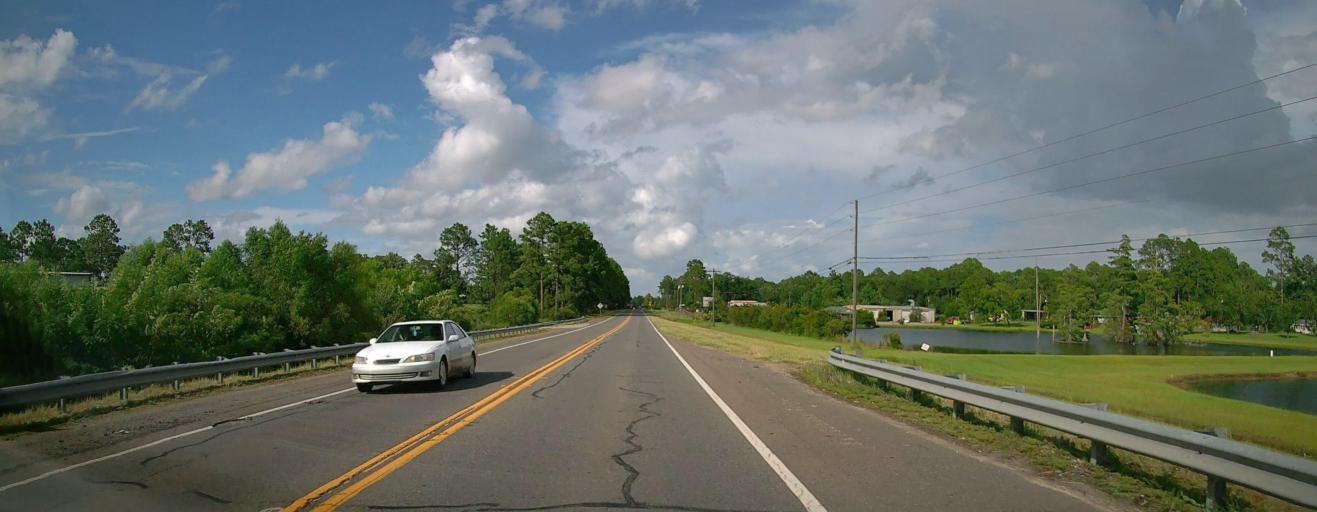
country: US
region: Georgia
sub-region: Coffee County
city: Douglas
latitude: 31.4618
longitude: -82.8856
